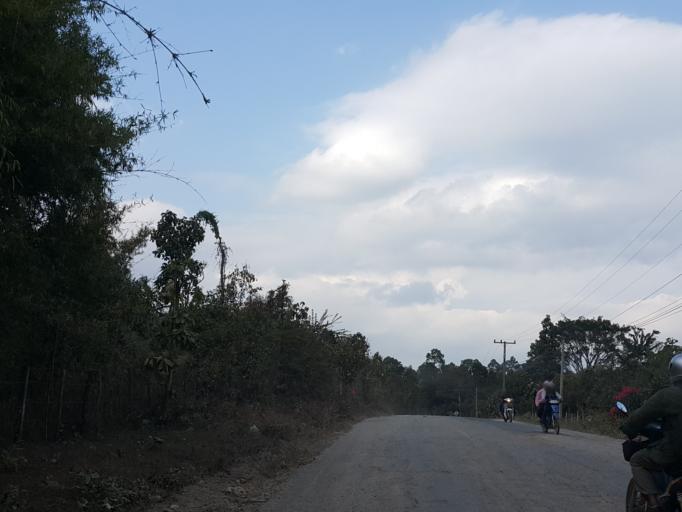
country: TH
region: Chiang Mai
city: Om Koi
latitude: 17.8060
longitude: 98.3321
